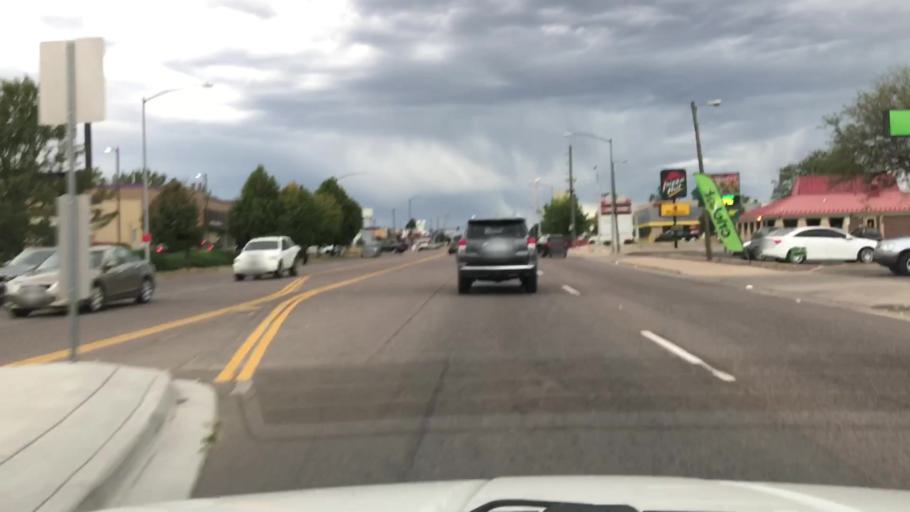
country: US
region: Colorado
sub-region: Adams County
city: Berkley
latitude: 39.7903
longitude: -105.0253
